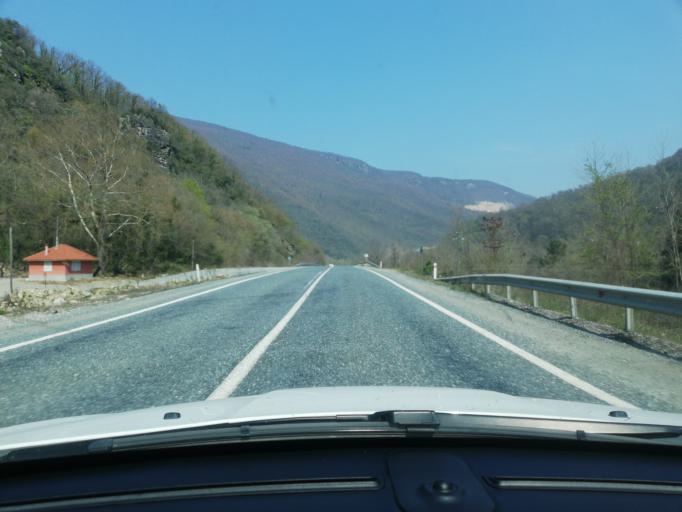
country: TR
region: Zonguldak
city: Gokcebey
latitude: 41.2587
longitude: 32.1556
